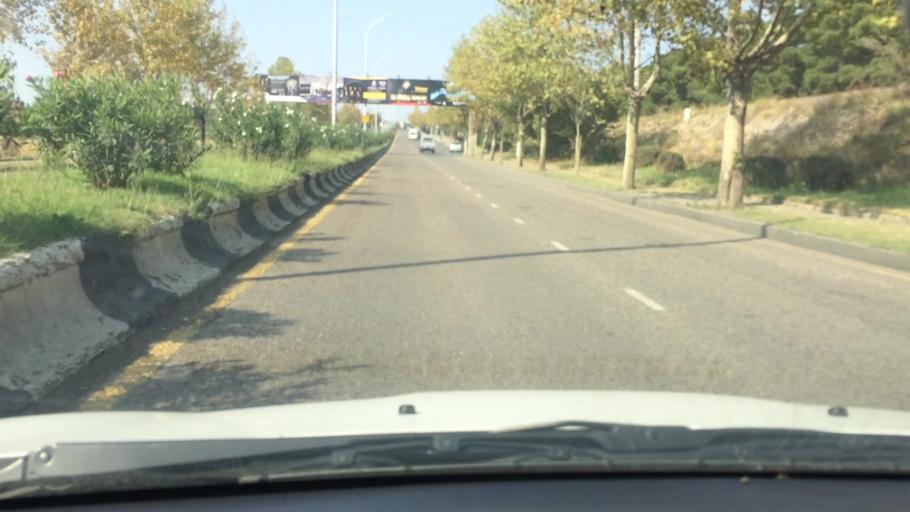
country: GE
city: Didi Lilo
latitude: 41.6808
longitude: 44.9572
